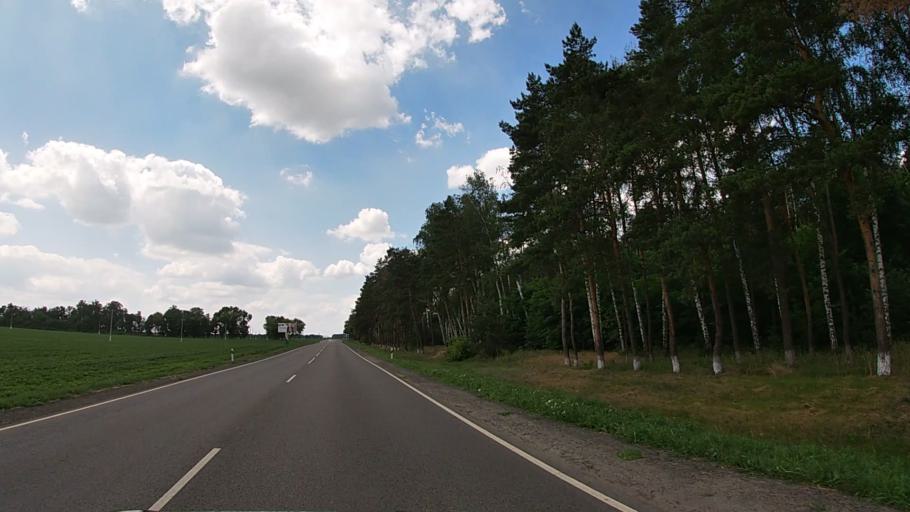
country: RU
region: Belgorod
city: Golovchino
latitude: 50.5071
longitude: 35.7451
